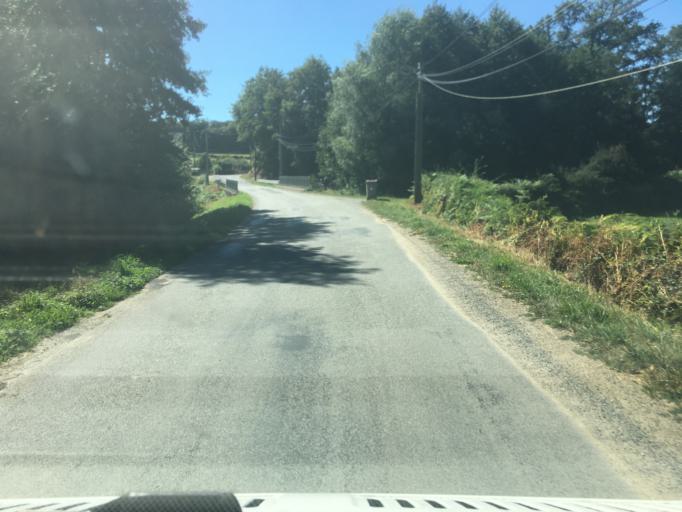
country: FR
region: Limousin
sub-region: Departement de la Correze
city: Bort-les-Orgues
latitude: 45.4411
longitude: 2.4726
